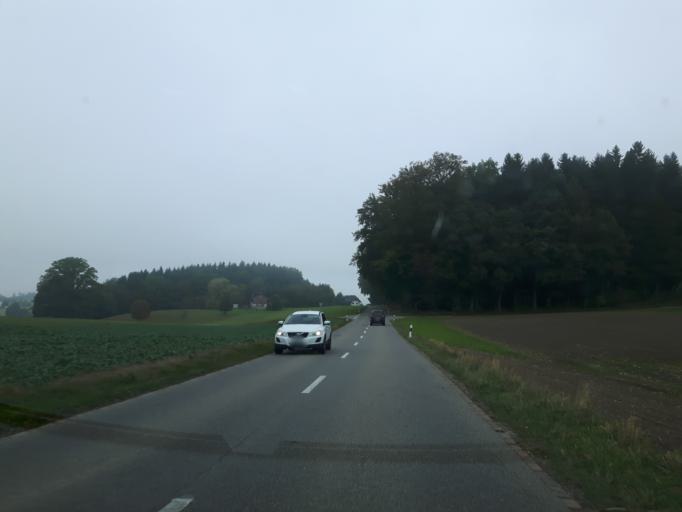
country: CH
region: Aargau
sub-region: Bezirk Zofingen
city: Brittnau
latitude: 47.2420
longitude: 7.9332
